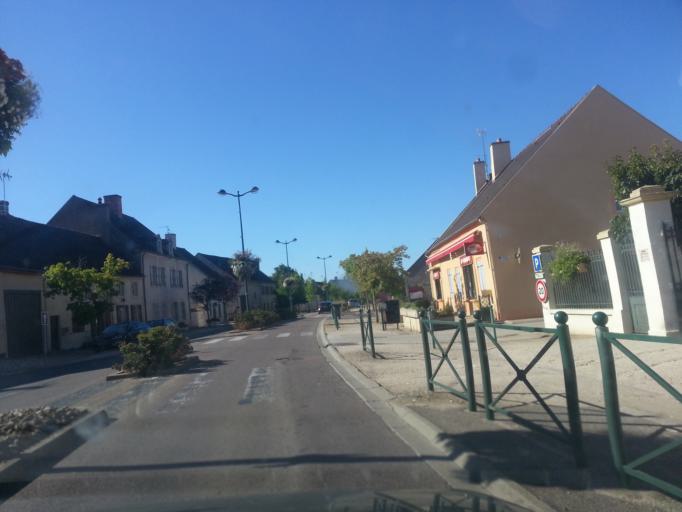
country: FR
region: Bourgogne
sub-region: Departement de Saone-et-Loire
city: Verdun-sur-le-Doubs
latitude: 46.8816
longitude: 5.0423
